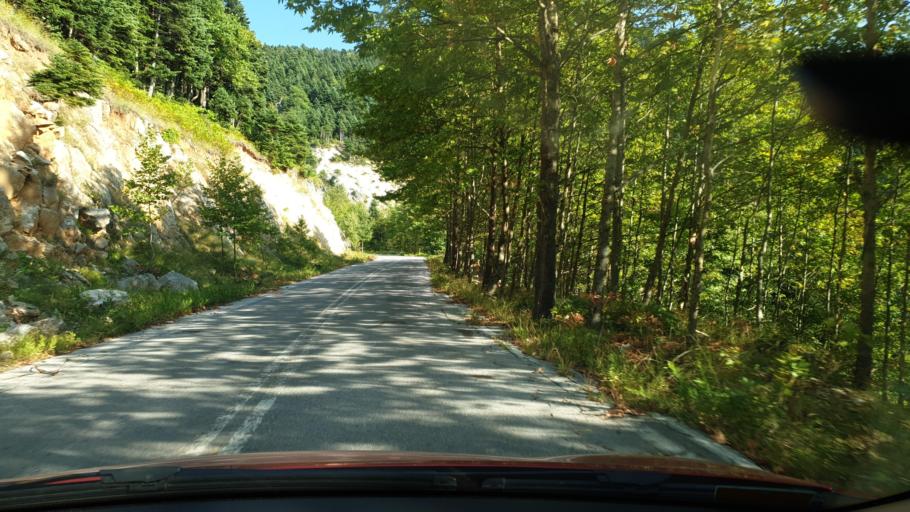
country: GR
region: Central Greece
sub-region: Nomos Evvoias
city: Yimnon
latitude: 38.6077
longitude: 23.9191
